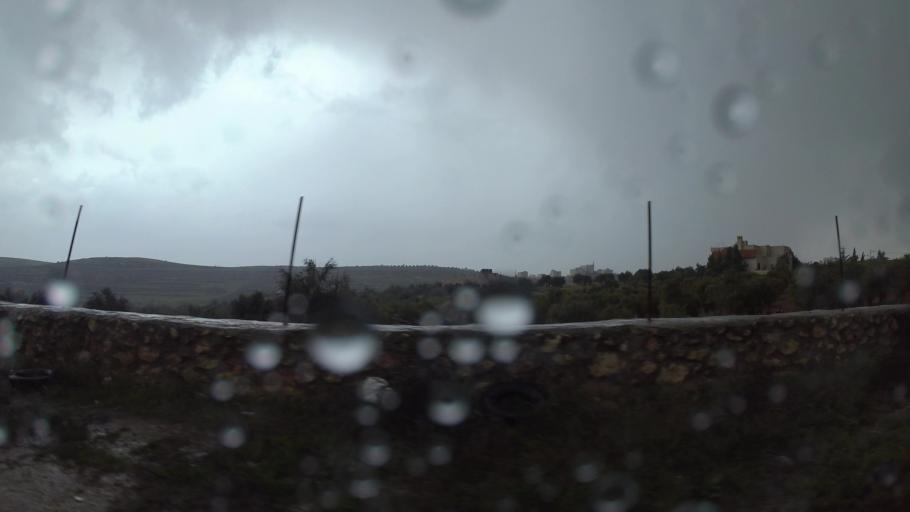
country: JO
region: Amman
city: Umm as Summaq
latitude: 31.8743
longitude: 35.8620
